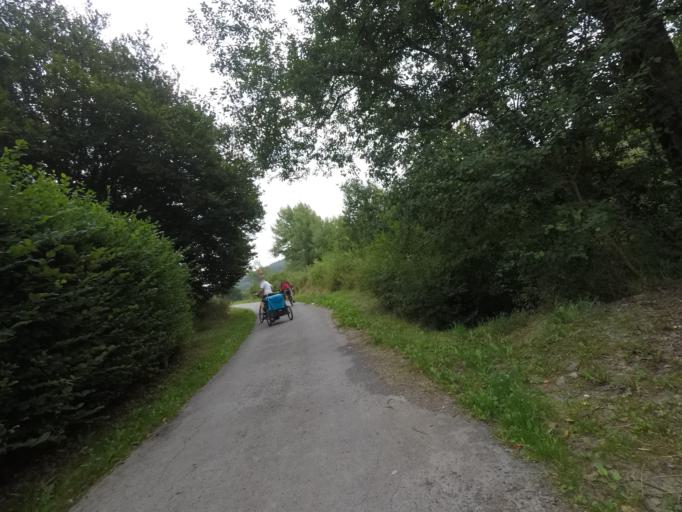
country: BE
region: Wallonia
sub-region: Province du Luxembourg
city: Martelange
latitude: 49.8450
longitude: 5.7164
